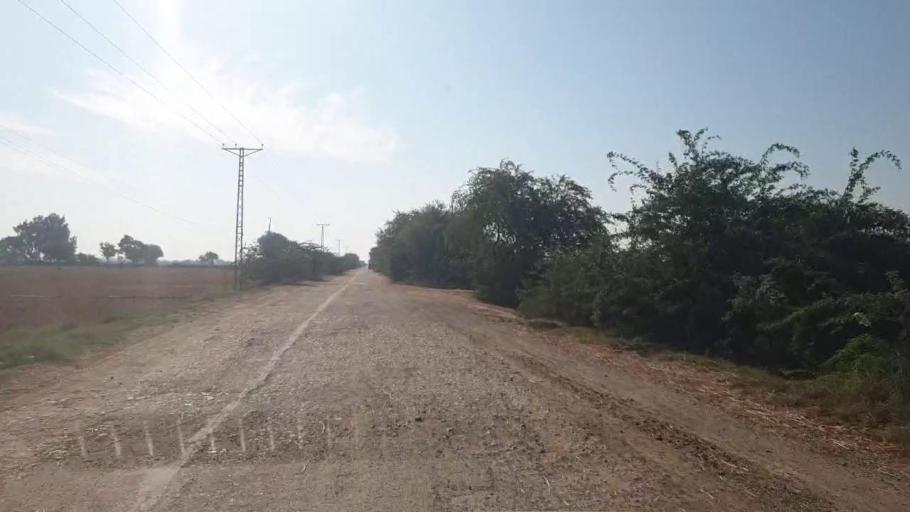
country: PK
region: Sindh
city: Talhar
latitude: 24.9187
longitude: 68.8149
